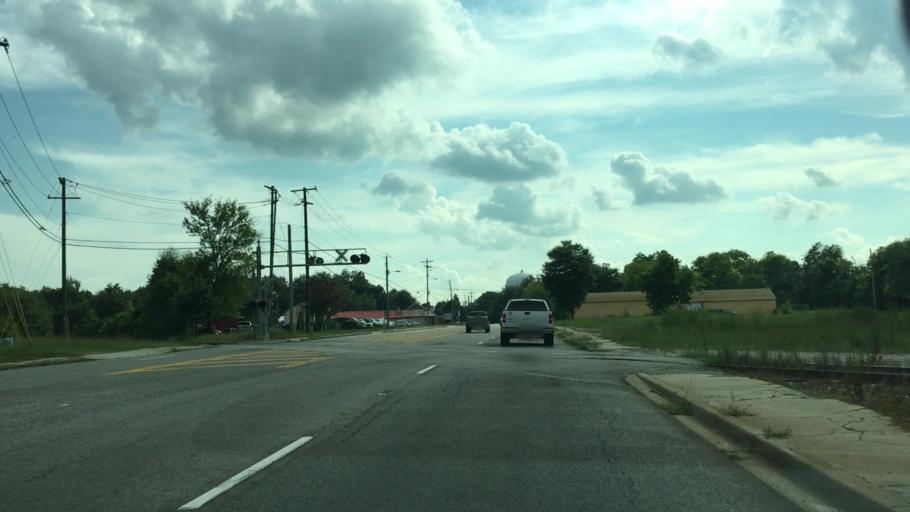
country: US
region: South Carolina
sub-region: Aiken County
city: Aiken
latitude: 33.5711
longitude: -81.7087
